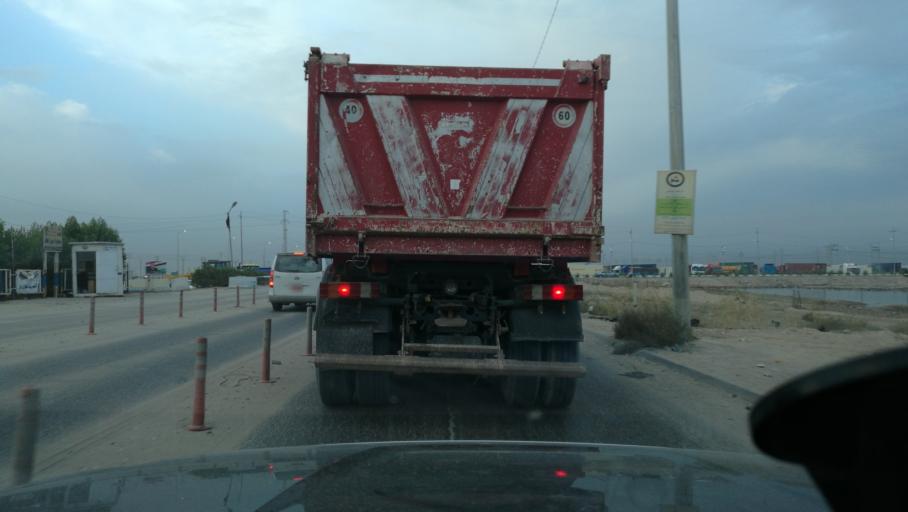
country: IQ
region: Basra Governorate
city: Al Harithah
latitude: 30.5413
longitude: 47.7421
